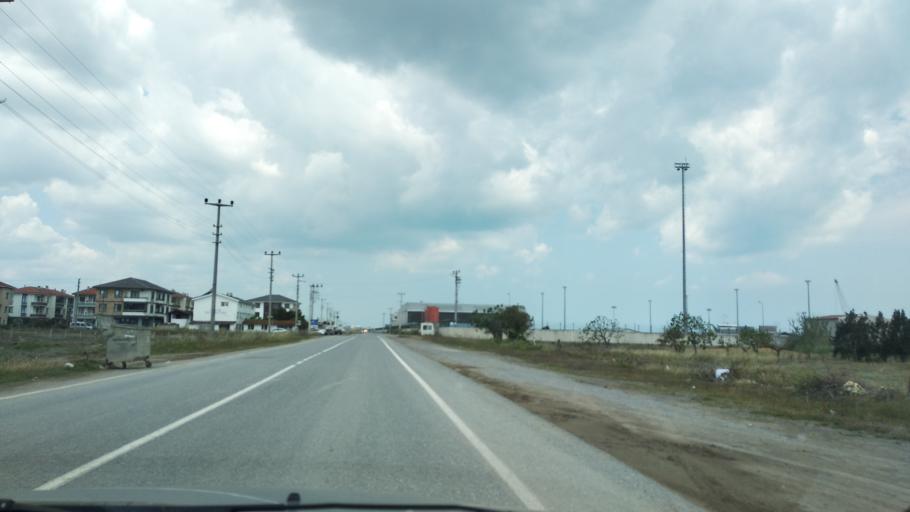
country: TR
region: Sakarya
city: Karasu
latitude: 41.1158
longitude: 30.6773
